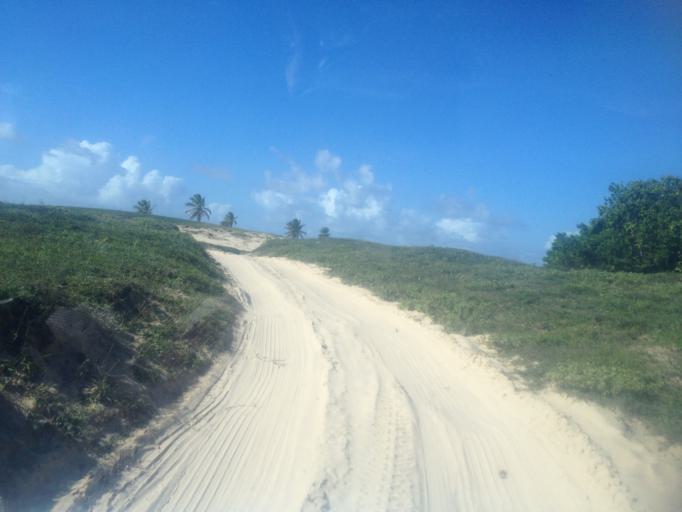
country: BR
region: Sergipe
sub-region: Indiaroba
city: Indiaroba
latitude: -11.4698
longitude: -37.3687
